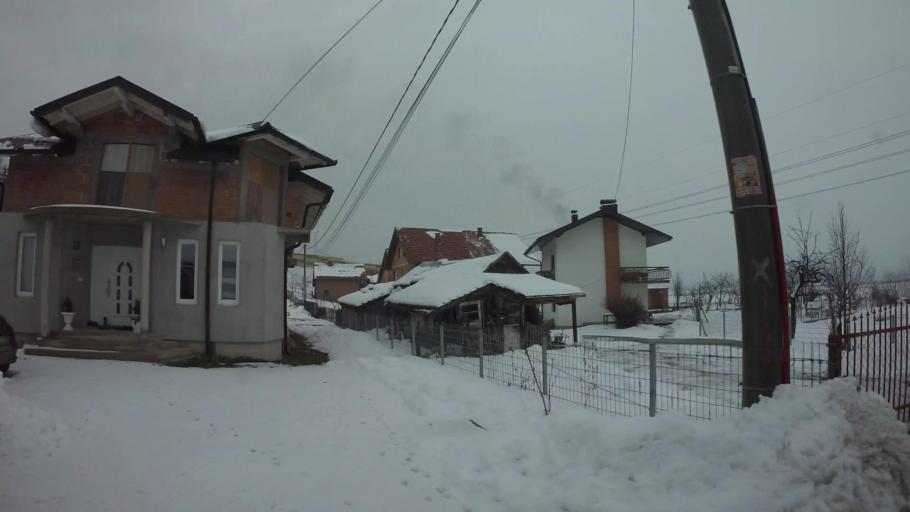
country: BA
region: Federation of Bosnia and Herzegovina
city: Hadzici
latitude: 43.8616
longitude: 18.2709
